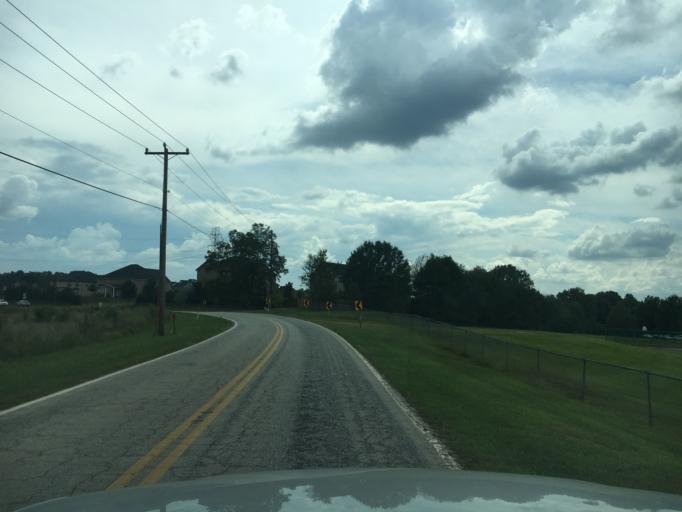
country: US
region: South Carolina
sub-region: Greenville County
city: Greer
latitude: 34.9035
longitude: -82.2454
